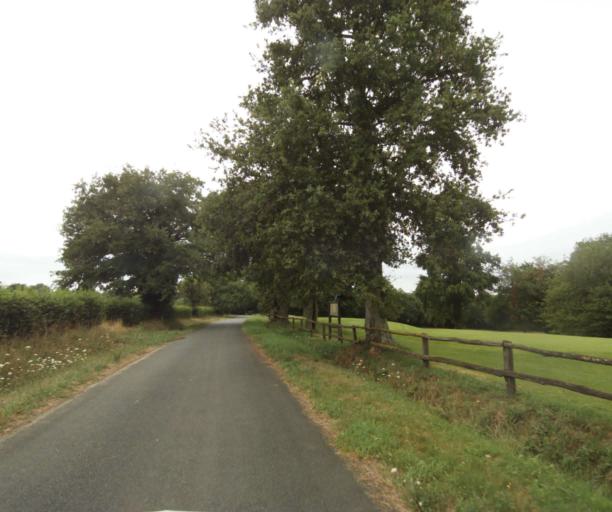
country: FR
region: Pays de la Loire
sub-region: Departement de la Sarthe
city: Sable-sur-Sarthe
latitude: 47.8195
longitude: -0.3636
